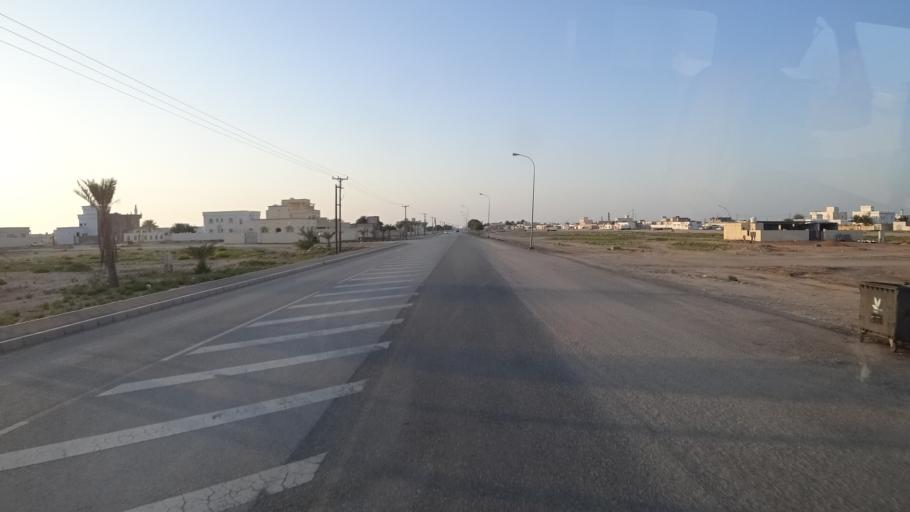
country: OM
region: Ash Sharqiyah
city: Sur
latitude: 22.5143
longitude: 59.7936
